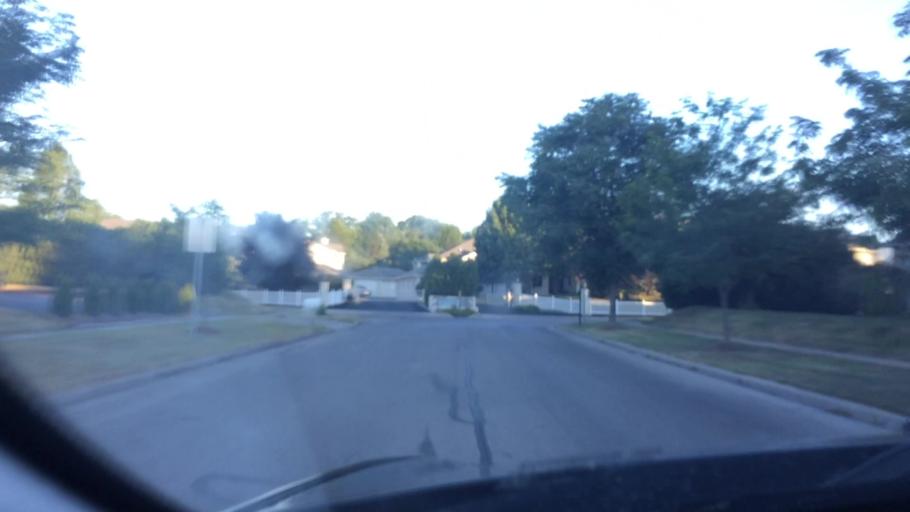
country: US
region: Ohio
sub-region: Lucas County
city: Ottawa Hills
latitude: 41.6493
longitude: -83.6565
